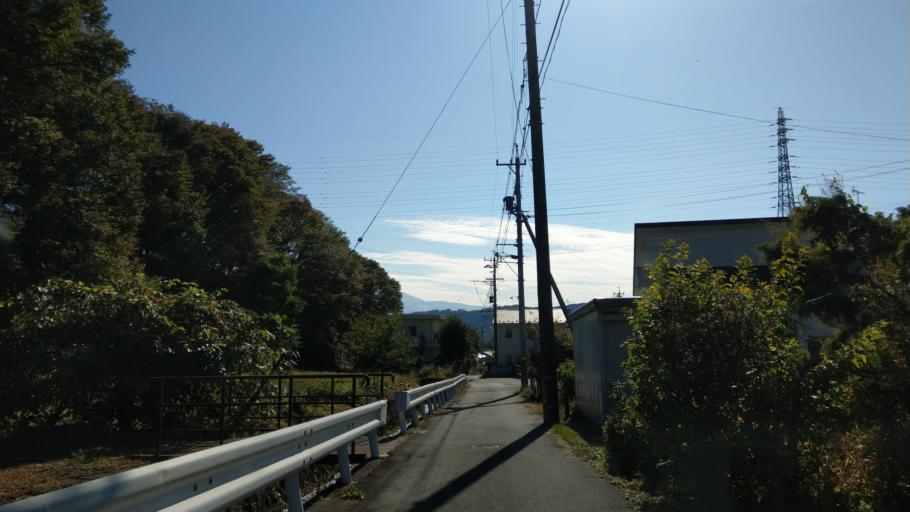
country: JP
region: Nagano
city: Komoro
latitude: 36.3344
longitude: 138.4319
